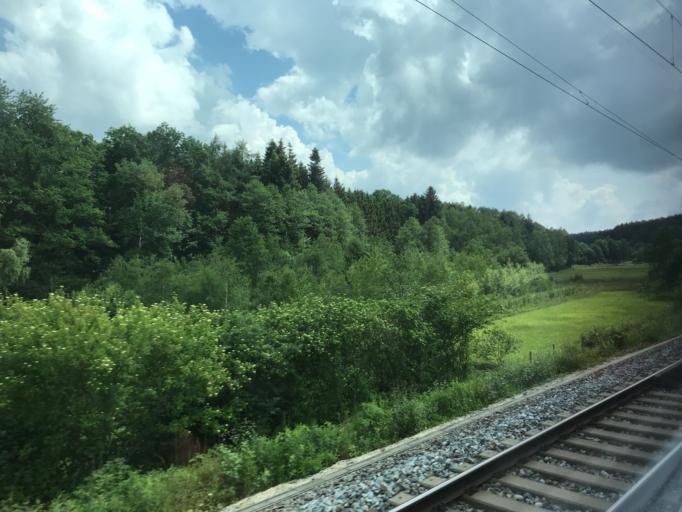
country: DE
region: Bavaria
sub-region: Swabia
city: Rosshaupten
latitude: 48.3879
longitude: 10.4970
